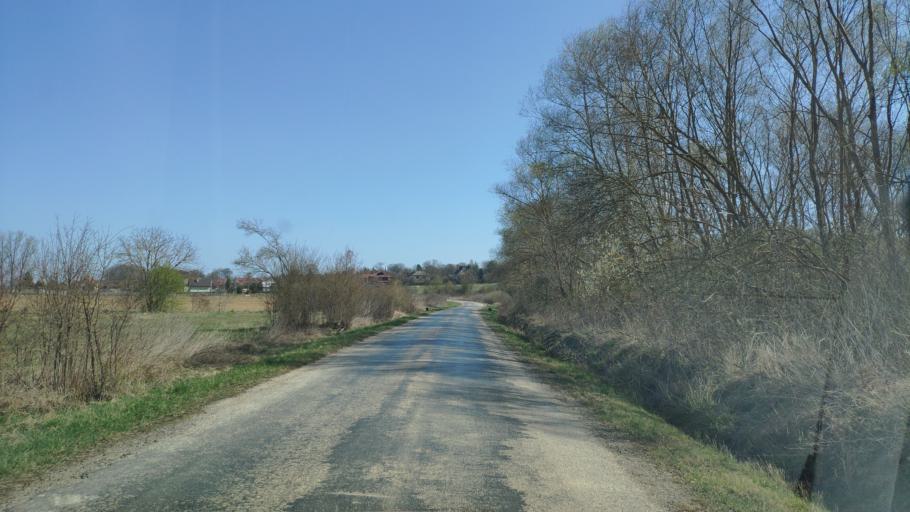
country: SK
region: Kosicky
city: Moldava nad Bodvou
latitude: 48.5612
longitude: 20.9536
